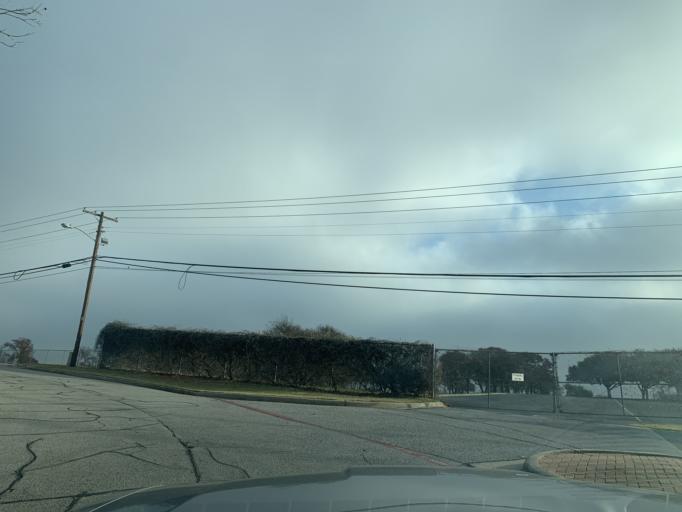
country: US
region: Texas
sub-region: Tarrant County
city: Bedford
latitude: 32.8405
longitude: -97.1404
